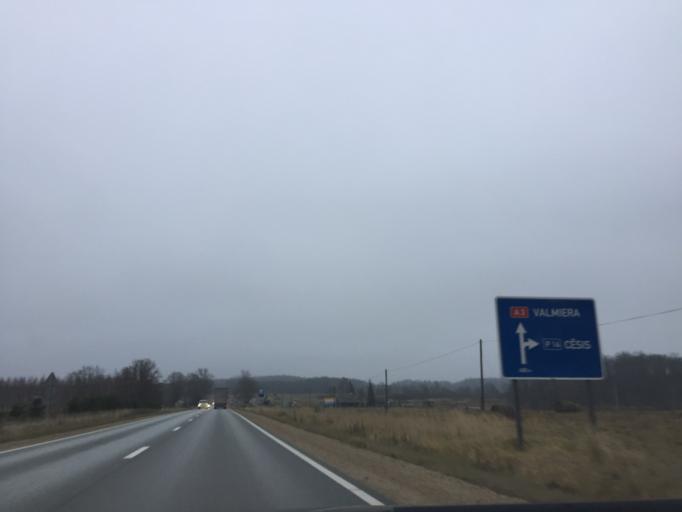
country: LV
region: Pargaujas
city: Stalbe
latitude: 57.3755
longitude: 25.0339
